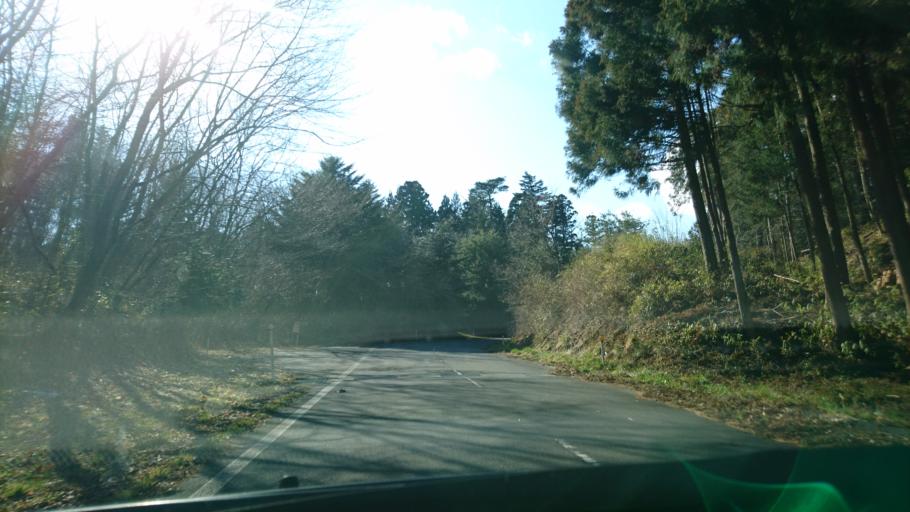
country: JP
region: Iwate
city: Ichinoseki
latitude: 38.8079
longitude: 141.2091
